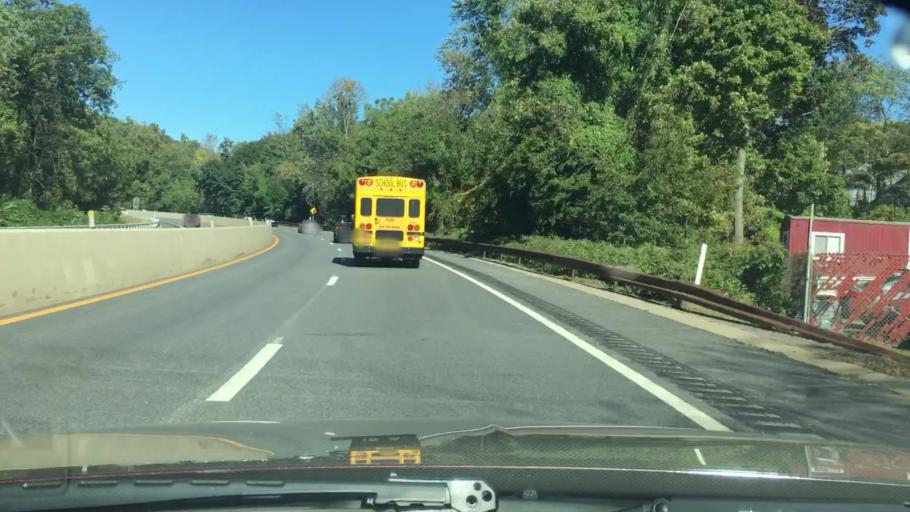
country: US
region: New York
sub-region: Westchester County
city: Pleasantville
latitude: 41.1369
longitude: -73.7936
